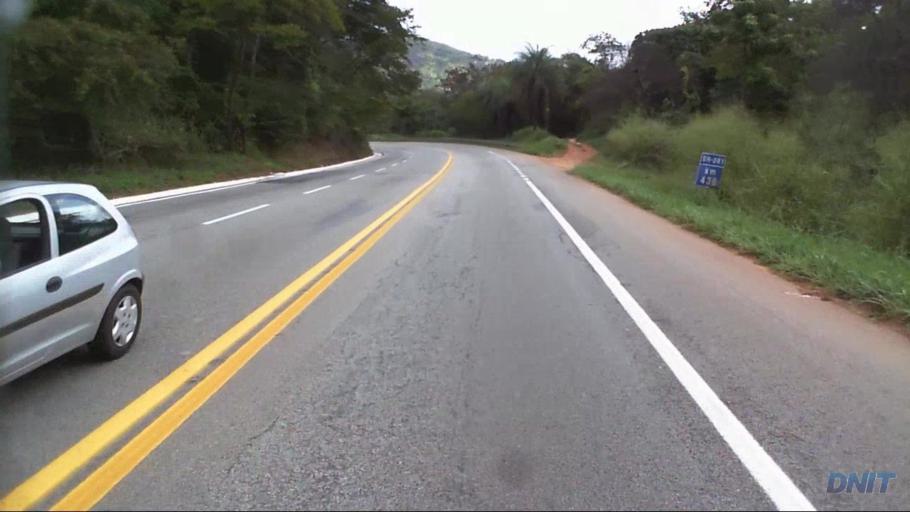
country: BR
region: Minas Gerais
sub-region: Santa Luzia
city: Santa Luzia
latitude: -19.7873
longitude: -43.7413
